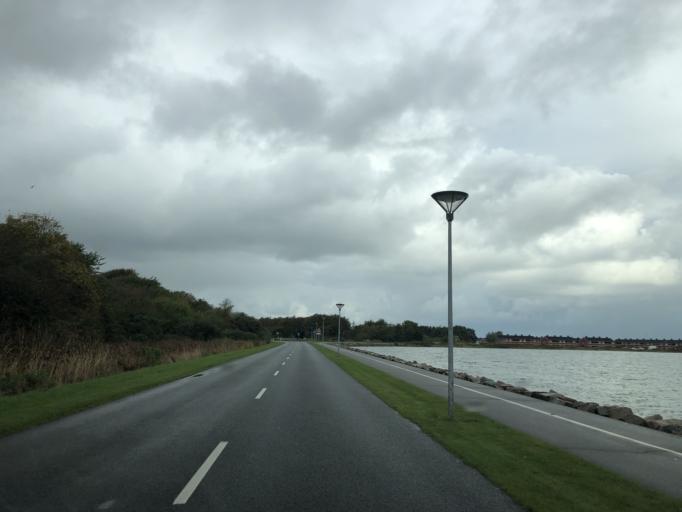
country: DK
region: Central Jutland
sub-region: Lemvig Kommune
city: Lemvig
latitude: 56.5601
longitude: 8.2948
